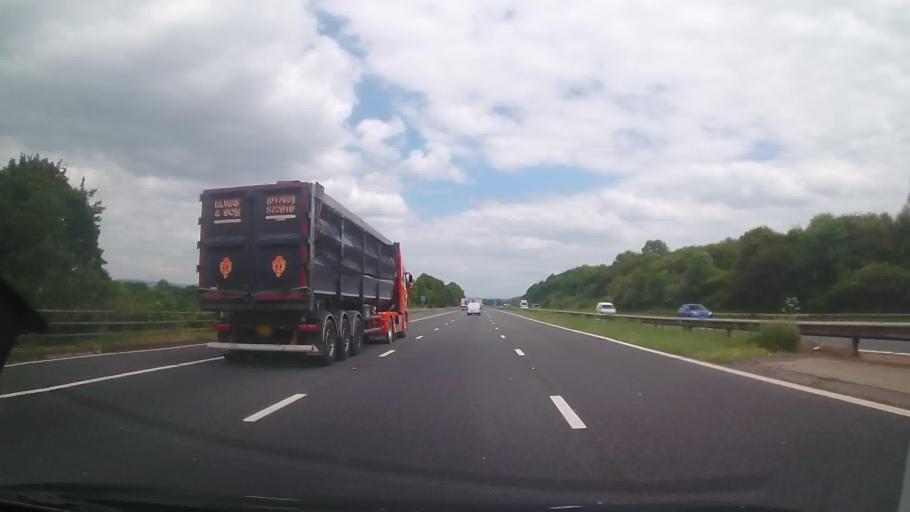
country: GB
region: England
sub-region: Somerset
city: Bishops Lydeard
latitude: 50.9670
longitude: -3.2092
